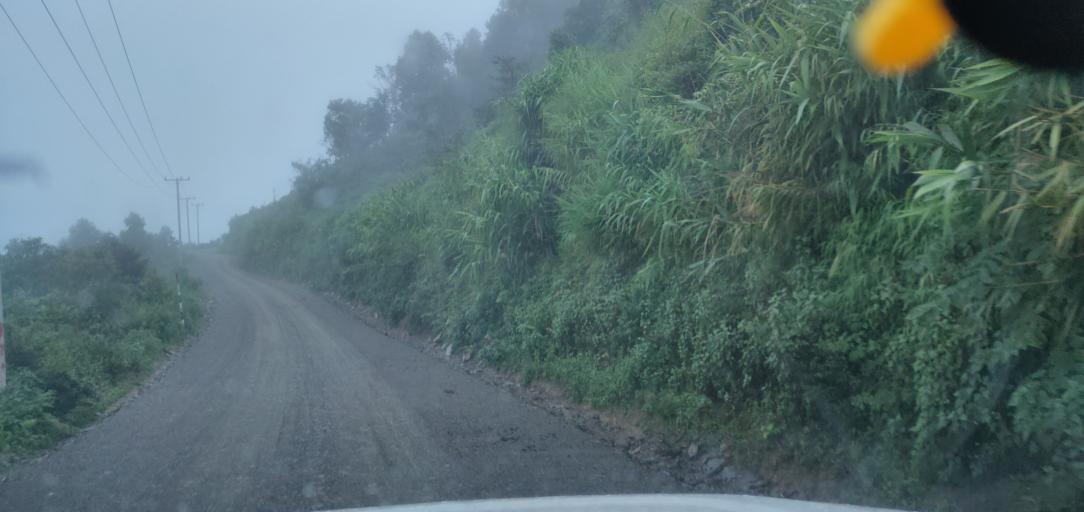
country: LA
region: Phongsali
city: Phongsali
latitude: 21.3978
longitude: 102.2215
